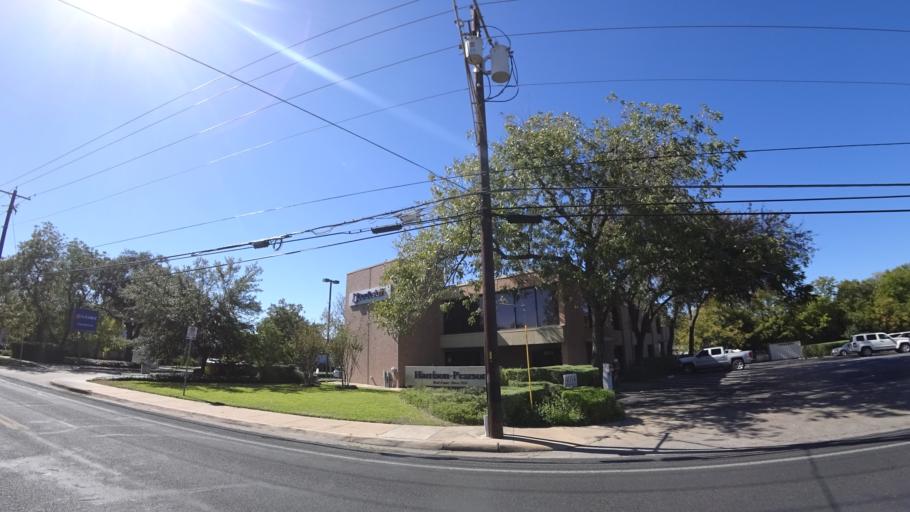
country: US
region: Texas
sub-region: Travis County
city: Austin
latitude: 30.3099
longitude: -97.7426
